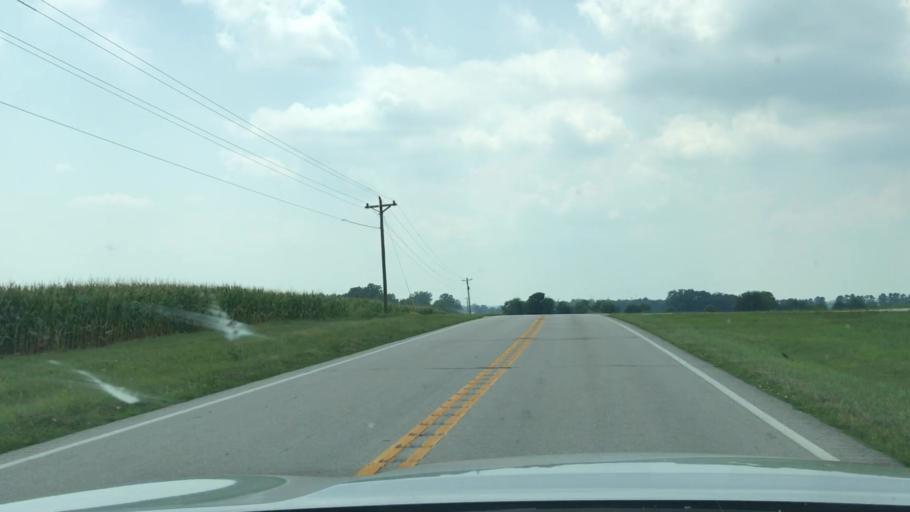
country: US
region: Kentucky
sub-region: Todd County
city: Guthrie
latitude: 36.6736
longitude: -87.1568
